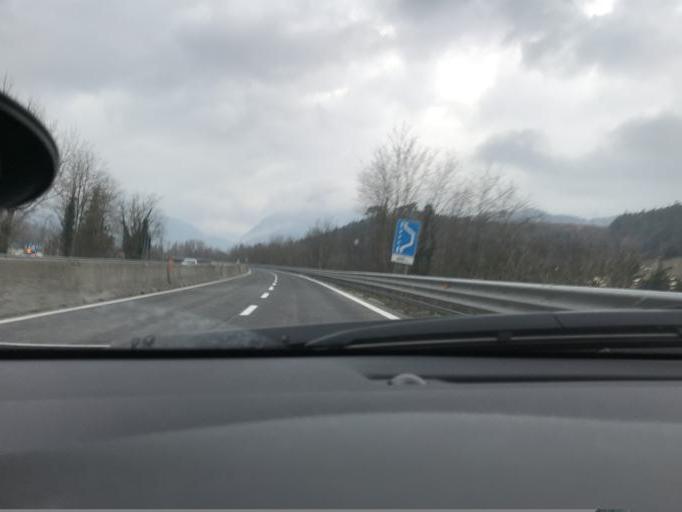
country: IT
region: The Marches
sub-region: Provincia di Ancona
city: Mergo
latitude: 43.4605
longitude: 13.0523
